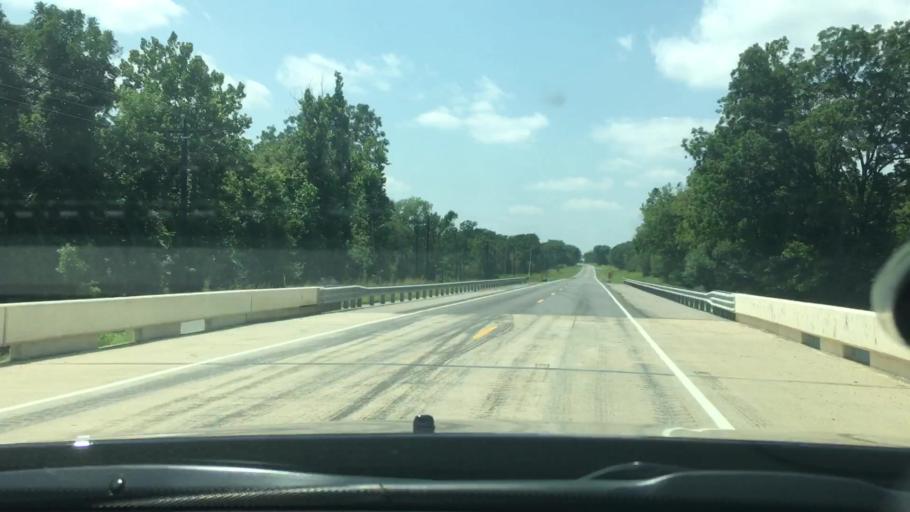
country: US
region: Oklahoma
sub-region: Atoka County
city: Atoka
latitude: 34.3791
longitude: -96.2791
